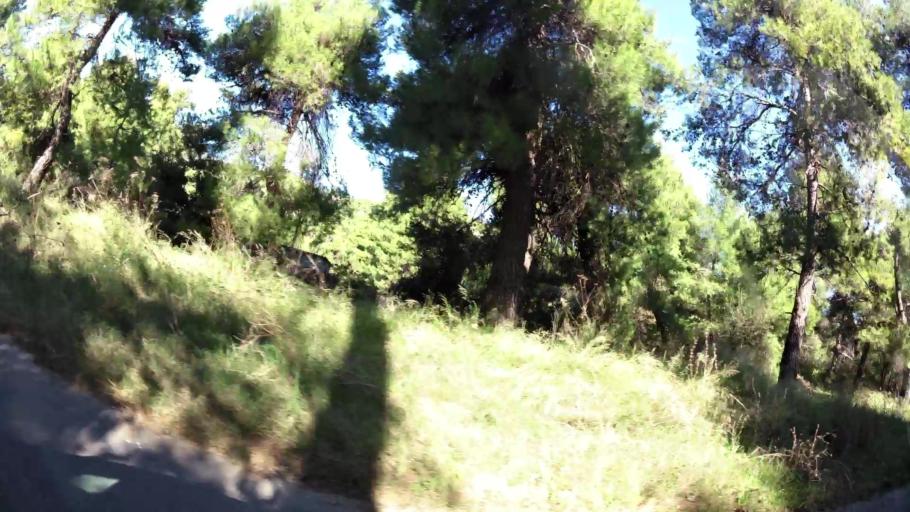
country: GR
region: Attica
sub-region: Nomarchia Anatolikis Attikis
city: Dionysos
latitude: 38.1013
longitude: 23.8760
